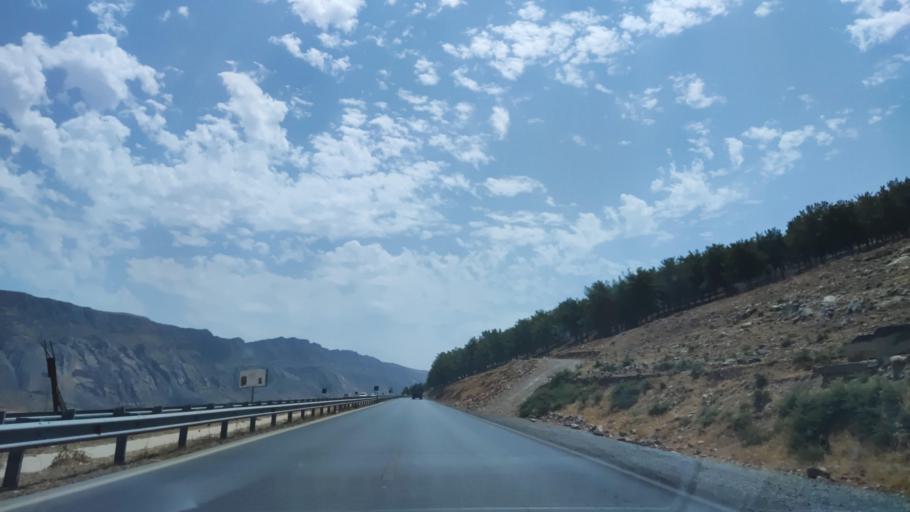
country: IQ
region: Arbil
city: Shaqlawah
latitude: 36.4913
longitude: 44.3741
